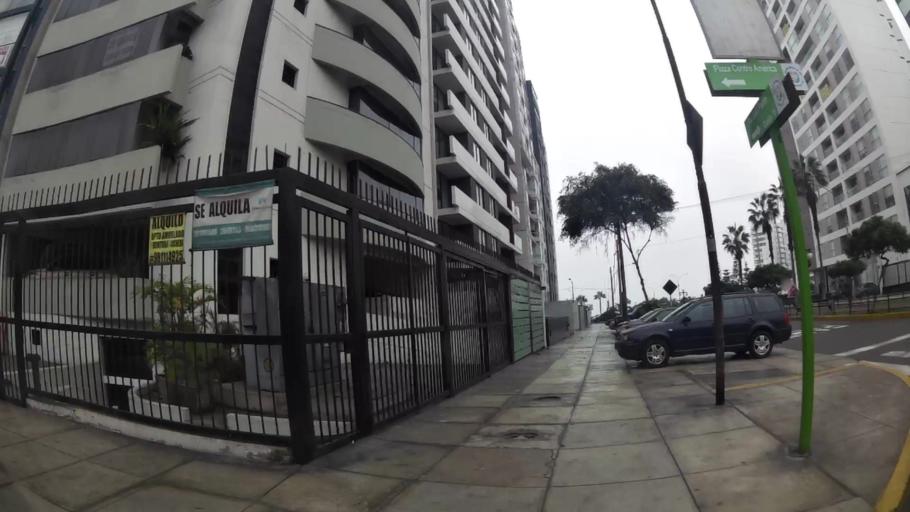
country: PE
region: Lima
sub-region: Lima
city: San Isidro
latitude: -12.1191
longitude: -77.0433
